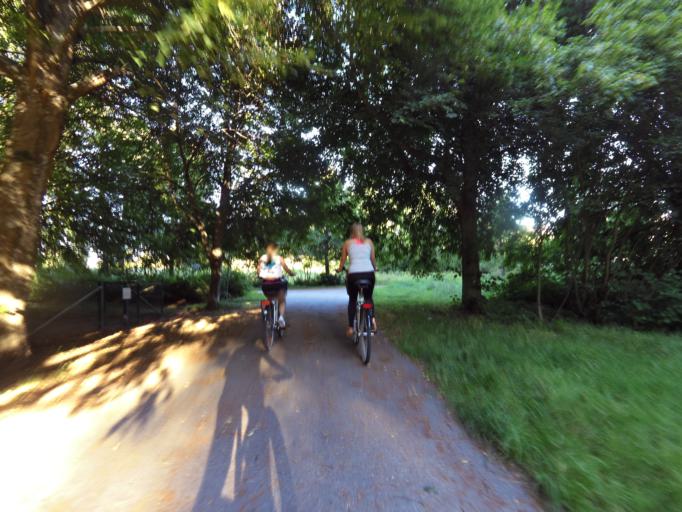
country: SE
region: Gaevleborg
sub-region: Gavle Kommun
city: Gavle
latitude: 60.6511
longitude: 17.1443
